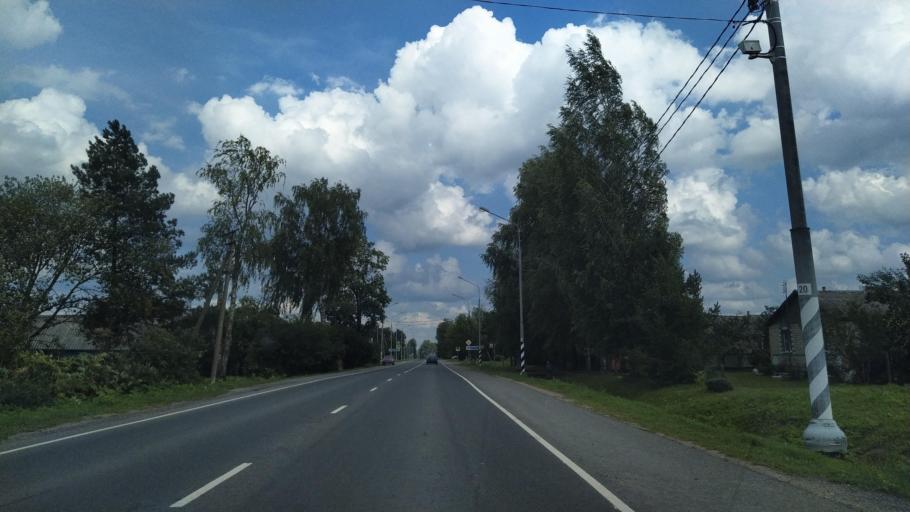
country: RU
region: Novgorod
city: Sol'tsy
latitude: 58.0815
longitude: 30.0951
